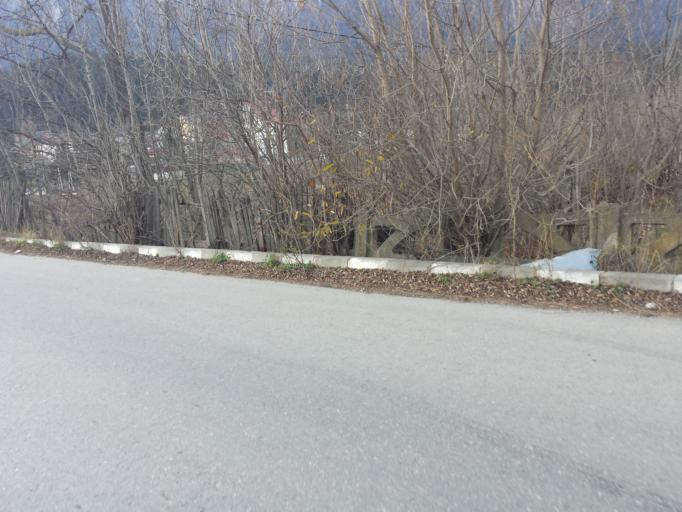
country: RO
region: Prahova
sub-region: Oras Busteni
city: Poiana Tapului
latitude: 45.3961
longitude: 25.5410
